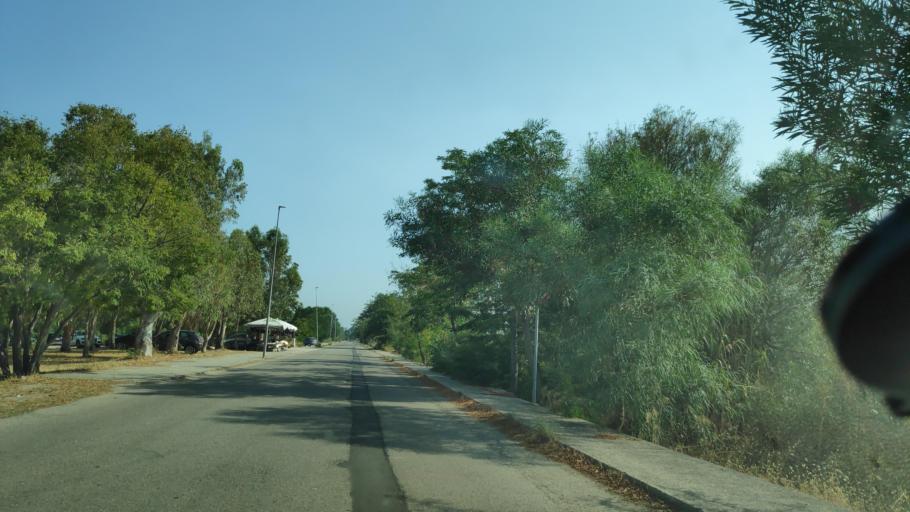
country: IT
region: Calabria
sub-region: Provincia di Catanzaro
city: Badolato Marina
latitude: 38.5786
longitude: 16.5679
